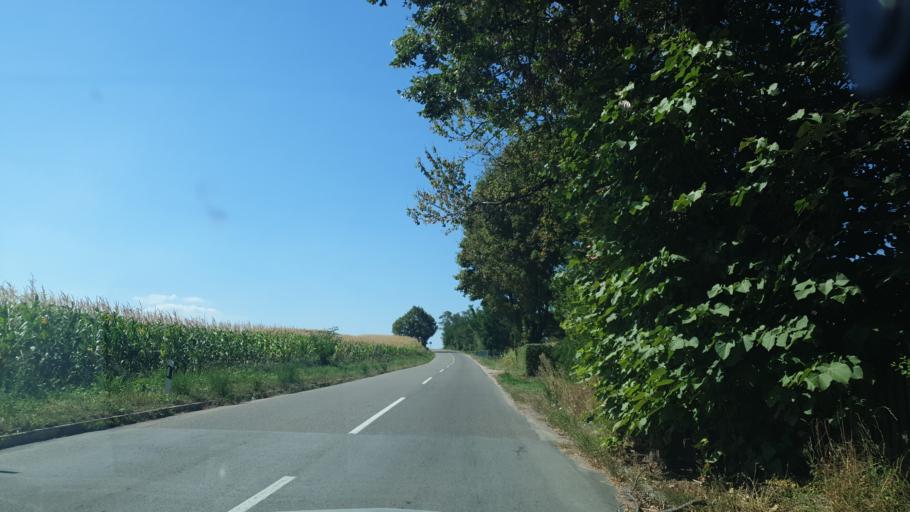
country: RS
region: Central Serbia
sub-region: Kolubarski Okrug
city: Mionica
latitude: 44.1759
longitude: 20.0330
